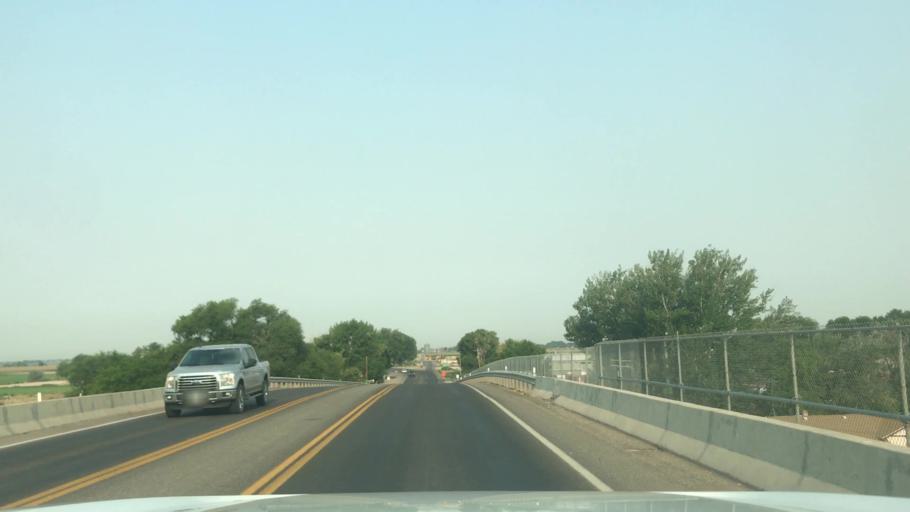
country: US
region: Utah
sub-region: Millard County
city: Delta
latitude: 39.3525
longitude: -112.5866
